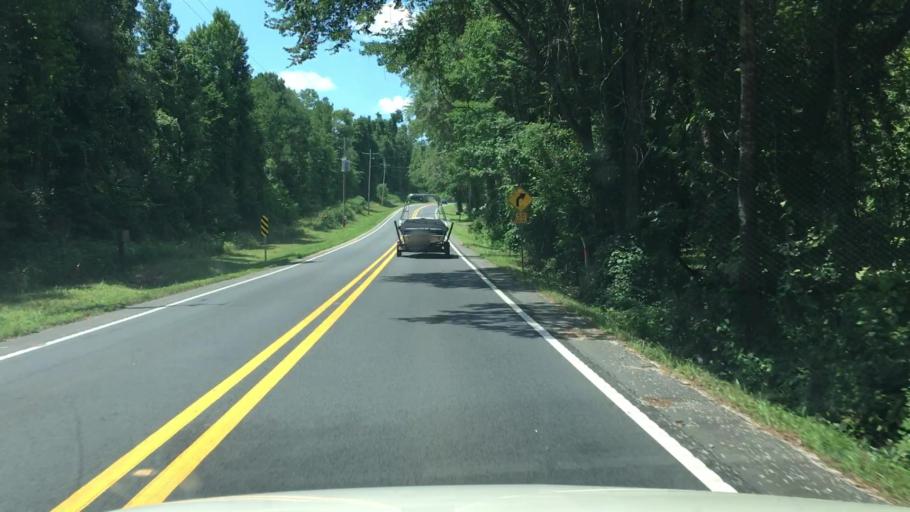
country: US
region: Arkansas
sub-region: Garland County
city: Lake Hamilton
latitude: 34.2715
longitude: -93.1471
